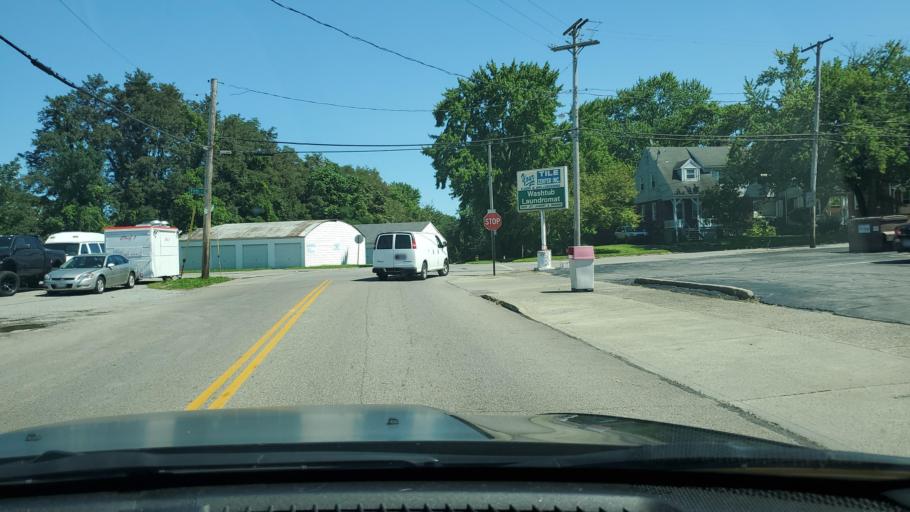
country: US
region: Ohio
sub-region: Mahoning County
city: Struthers
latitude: 41.0607
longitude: -80.6041
